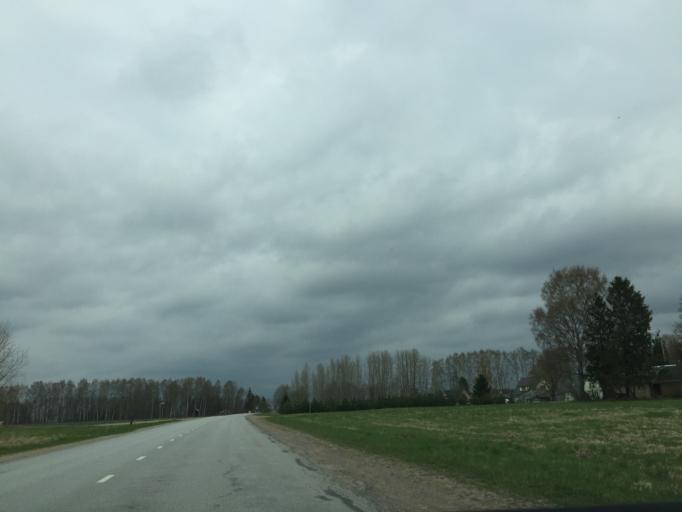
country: EE
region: Tartu
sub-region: Noo vald
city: Noo
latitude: 58.2772
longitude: 26.5301
